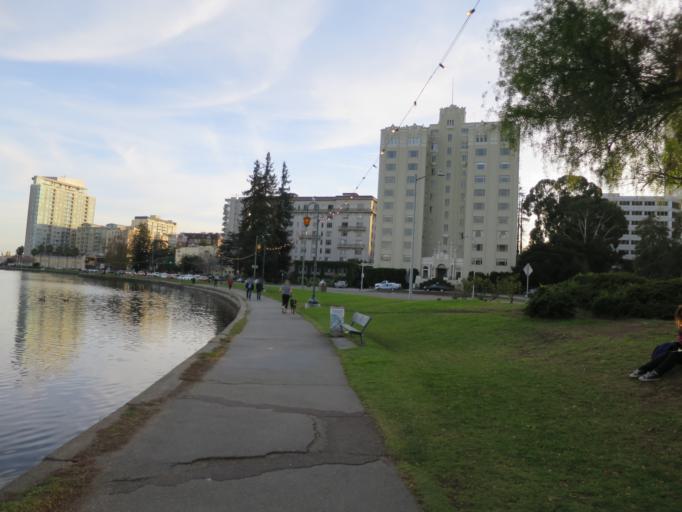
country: US
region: California
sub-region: Alameda County
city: Oakland
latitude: 37.8076
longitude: -122.2631
